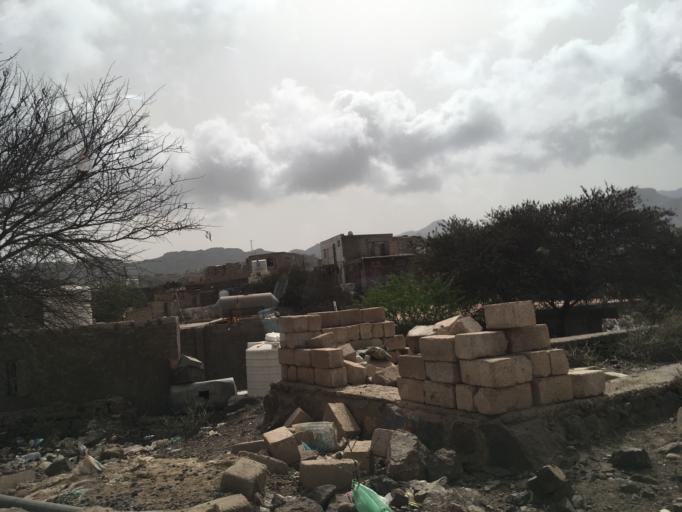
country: YE
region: Ad Dali'
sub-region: Ad Dhale'e
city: Dhalie
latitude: 13.7075
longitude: 44.7362
